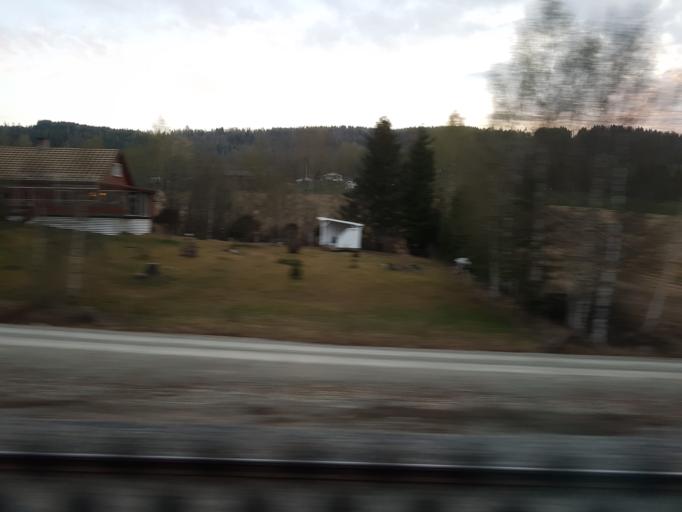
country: NO
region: Hedmark
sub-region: Ringsaker
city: Moelv
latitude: 60.9157
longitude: 10.8179
